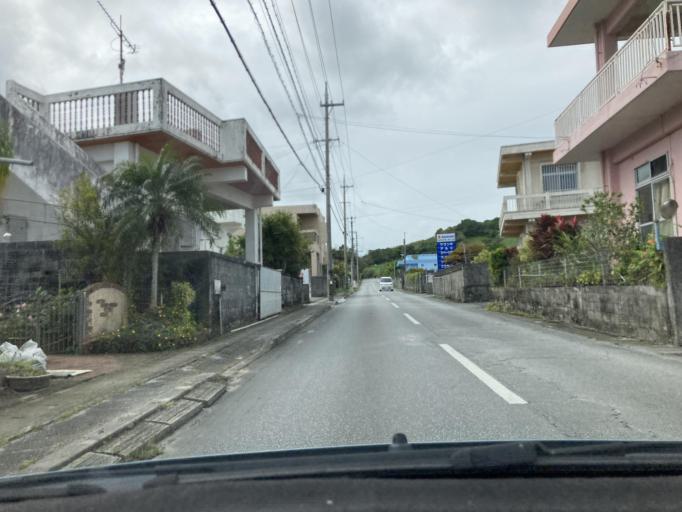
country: JP
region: Okinawa
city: Ginowan
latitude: 26.2318
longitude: 127.7438
